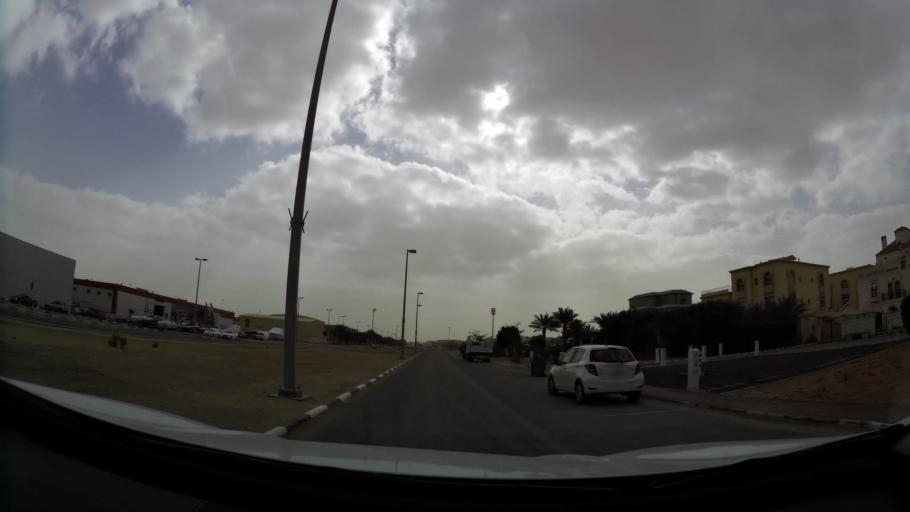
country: AE
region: Abu Dhabi
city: Abu Dhabi
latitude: 24.4152
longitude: 54.4963
